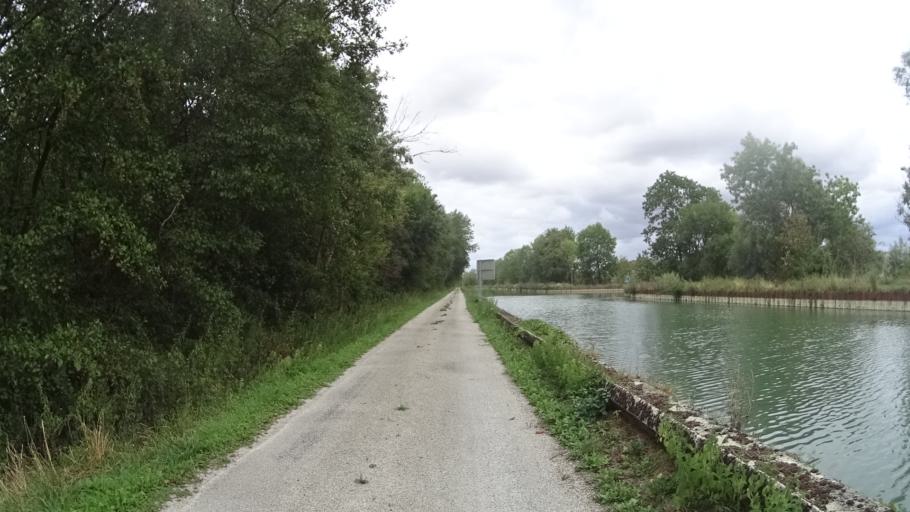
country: FR
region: Picardie
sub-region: Departement de l'Aisne
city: La Fere
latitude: 49.6915
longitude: 3.3684
